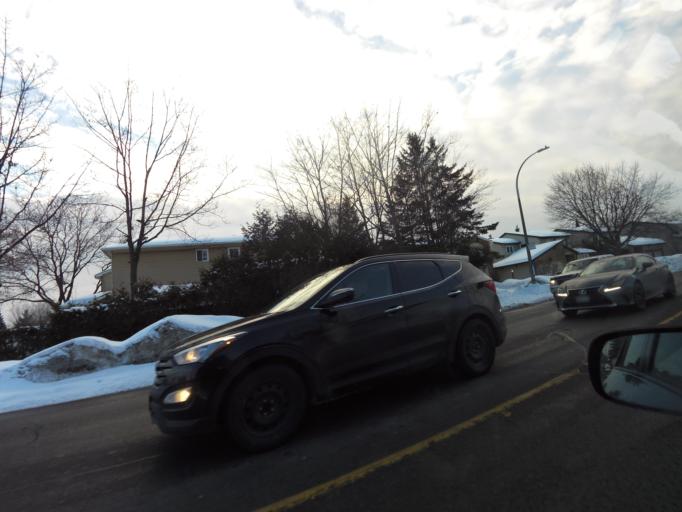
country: CA
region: Quebec
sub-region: Outaouais
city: Gatineau
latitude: 45.4530
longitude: -75.5406
